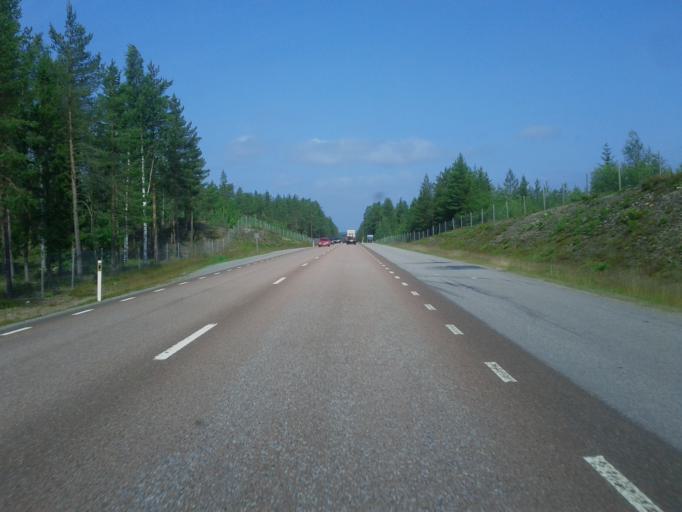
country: SE
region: Vaesterbotten
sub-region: Skelleftea Kommun
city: Burea
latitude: 64.5929
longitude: 21.2116
